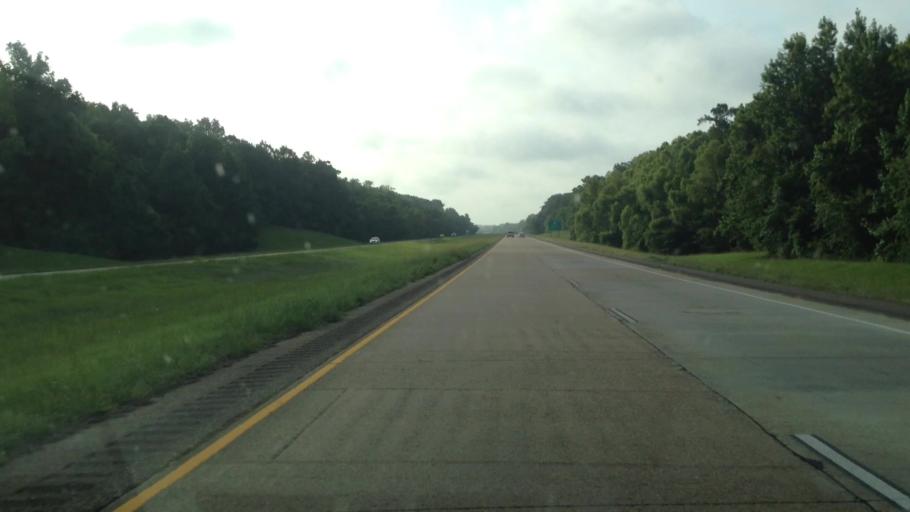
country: US
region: Louisiana
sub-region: Rapides Parish
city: Lecompte
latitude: 31.0248
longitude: -92.3986
